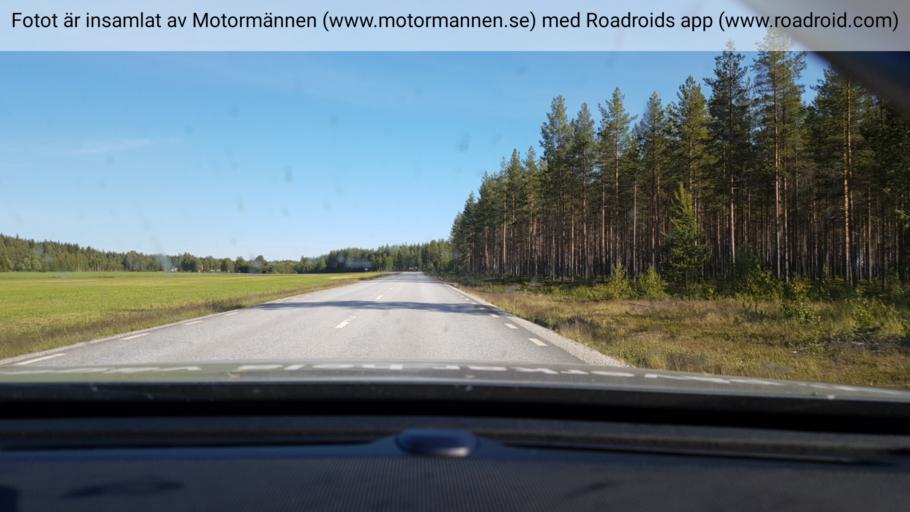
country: SE
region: Vaesterbotten
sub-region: Vindelns Kommun
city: Vindeln
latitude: 64.1176
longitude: 19.5662
